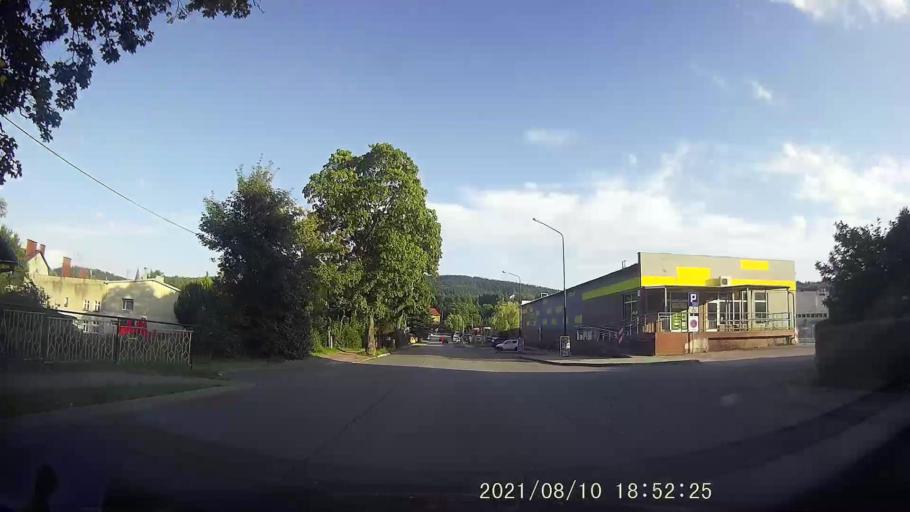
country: PL
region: Lower Silesian Voivodeship
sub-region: Powiat klodzki
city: Duszniki-Zdroj
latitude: 50.4074
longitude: 16.3846
